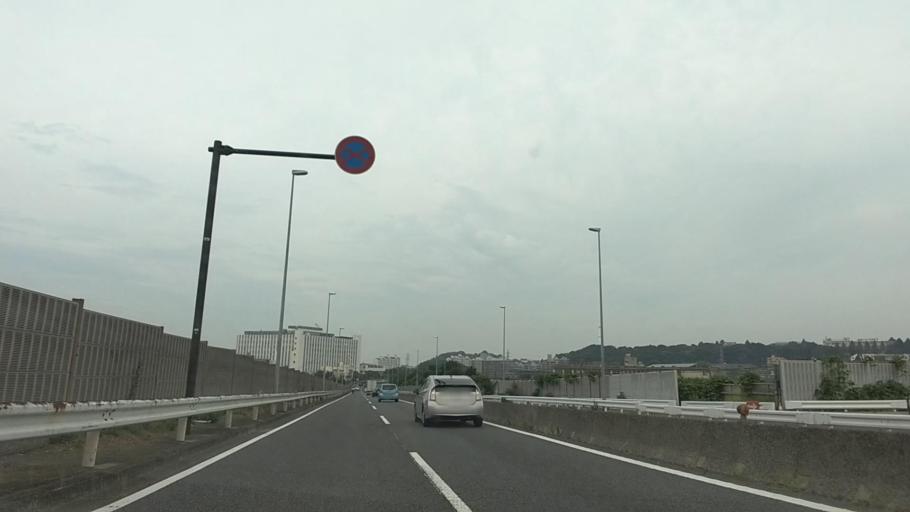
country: JP
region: Kanagawa
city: Fujisawa
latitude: 35.3548
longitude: 139.4867
